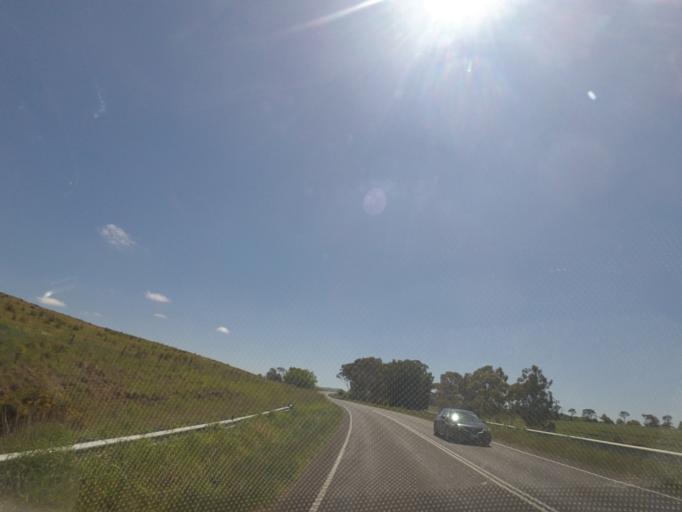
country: AU
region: Victoria
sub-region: Hume
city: Sunbury
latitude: -37.4652
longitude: 144.7442
